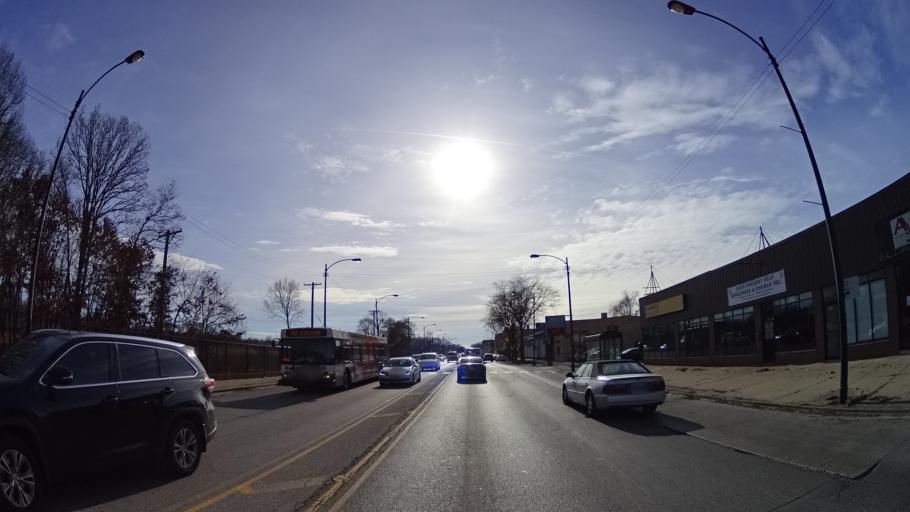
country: US
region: Illinois
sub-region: Cook County
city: Lincolnwood
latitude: 41.9854
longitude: -87.6895
